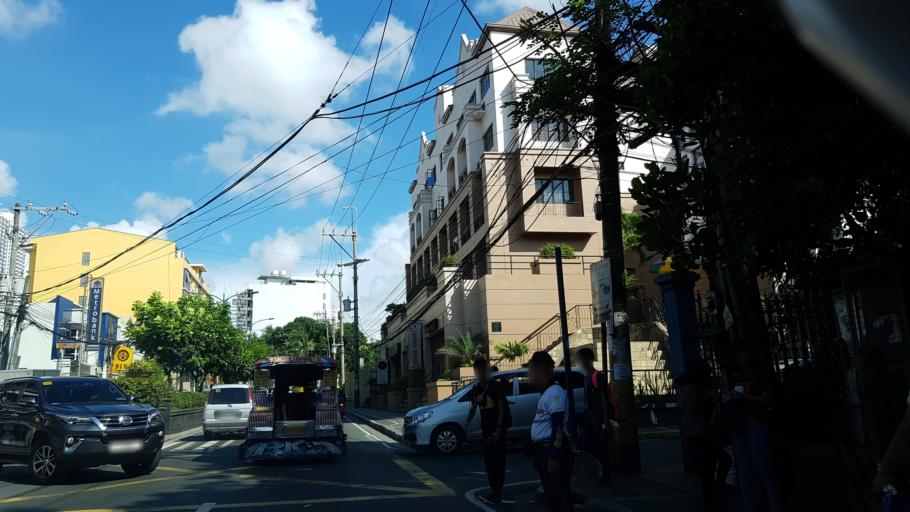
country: PH
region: Metro Manila
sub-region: Mandaluyong
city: Mandaluyong City
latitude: 14.5746
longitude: 121.0428
